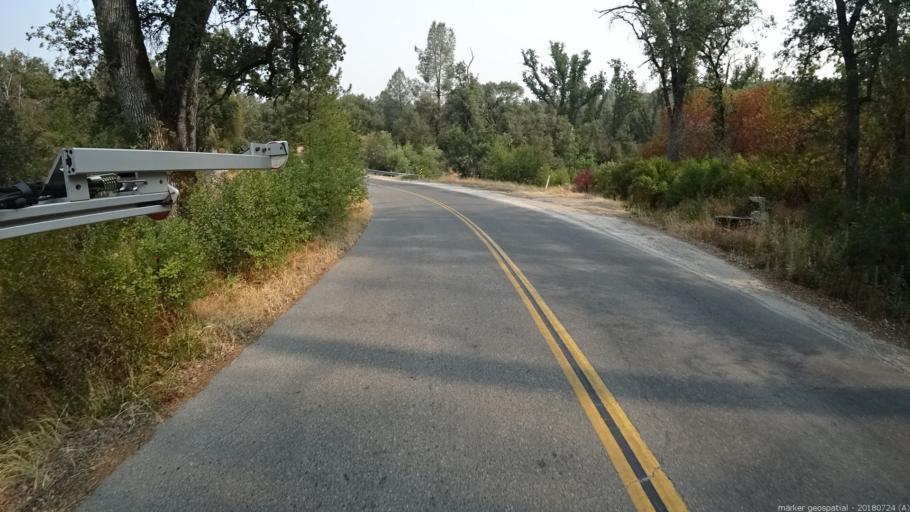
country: US
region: California
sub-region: Madera County
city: Oakhurst
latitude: 37.3073
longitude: -119.6186
